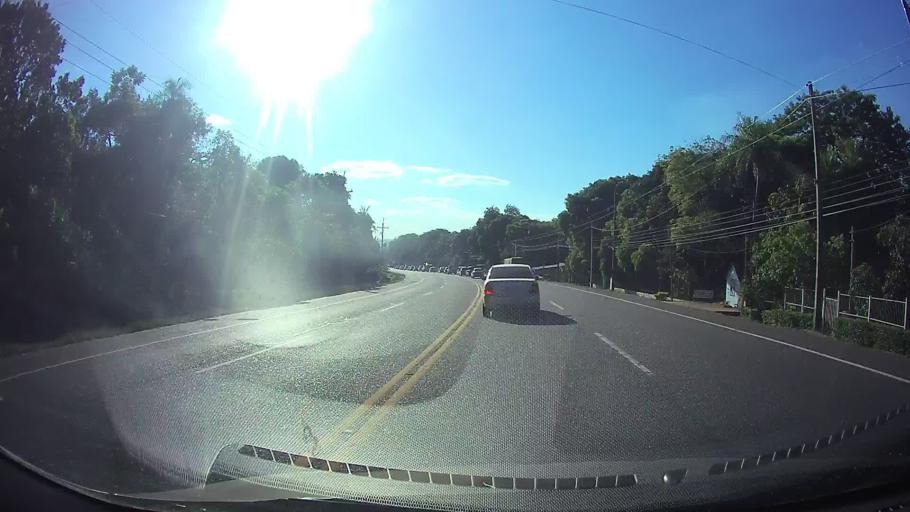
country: PY
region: Cordillera
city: Caacupe
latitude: -25.3724
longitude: -57.2102
